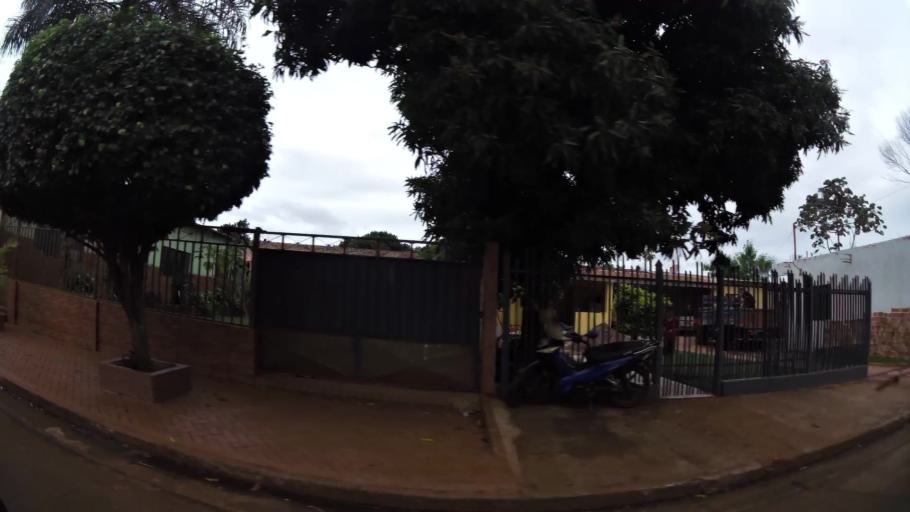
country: PY
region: Alto Parana
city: Ciudad del Este
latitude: -25.4033
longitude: -54.6272
